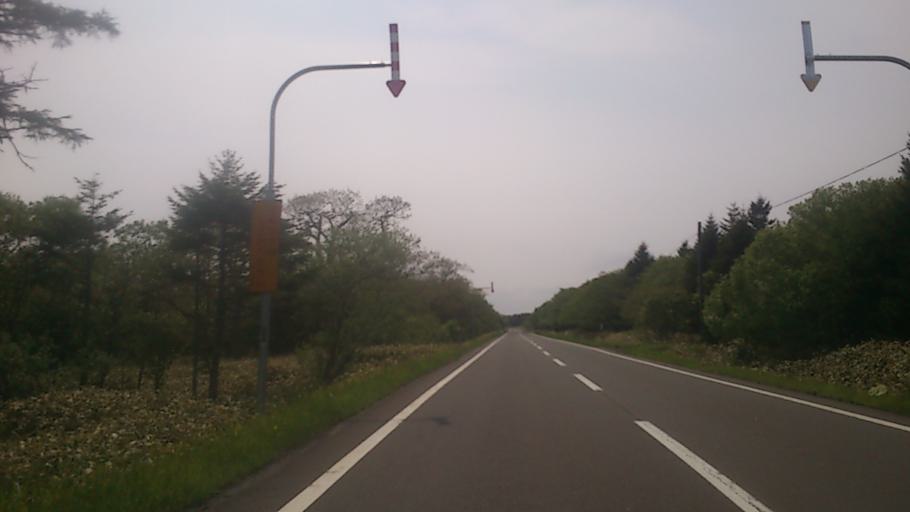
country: JP
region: Hokkaido
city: Nemuro
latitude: 43.2138
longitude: 145.3783
